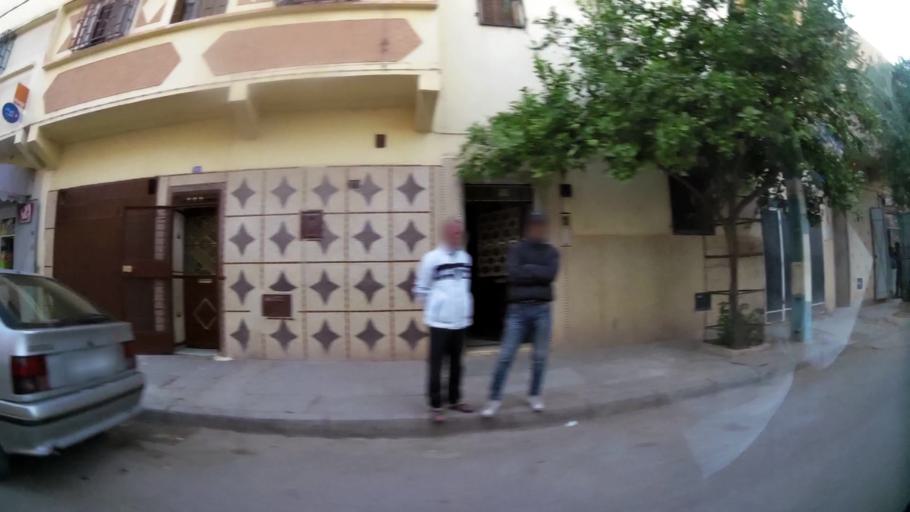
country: MA
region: Oriental
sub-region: Oujda-Angad
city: Oujda
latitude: 34.6982
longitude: -1.9231
